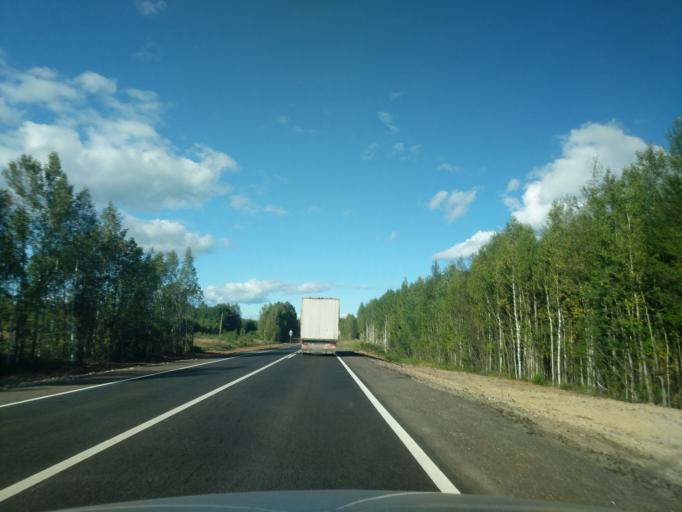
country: RU
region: Kostroma
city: Makar'yev
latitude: 57.9896
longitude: 43.9660
